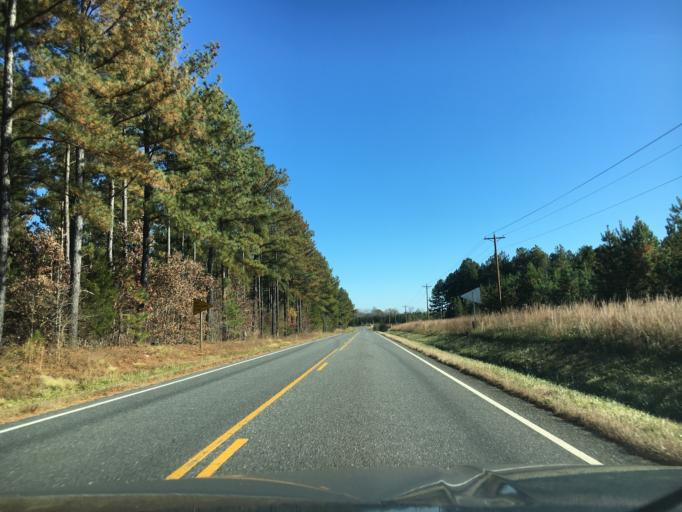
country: US
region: Virginia
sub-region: Buckingham County
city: Buckingham
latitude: 37.4993
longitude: -78.6228
